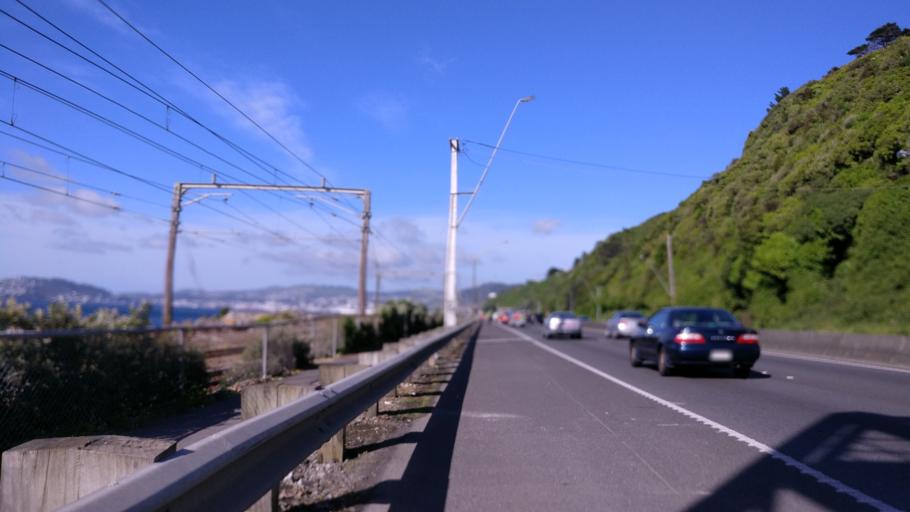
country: NZ
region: Wellington
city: Petone
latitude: -41.2413
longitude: 174.8241
